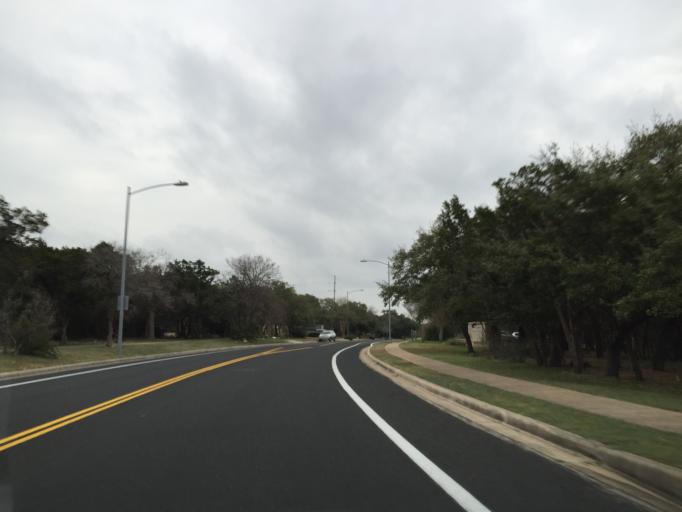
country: US
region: Texas
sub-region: Travis County
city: Barton Creek
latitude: 30.2495
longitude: -97.8422
